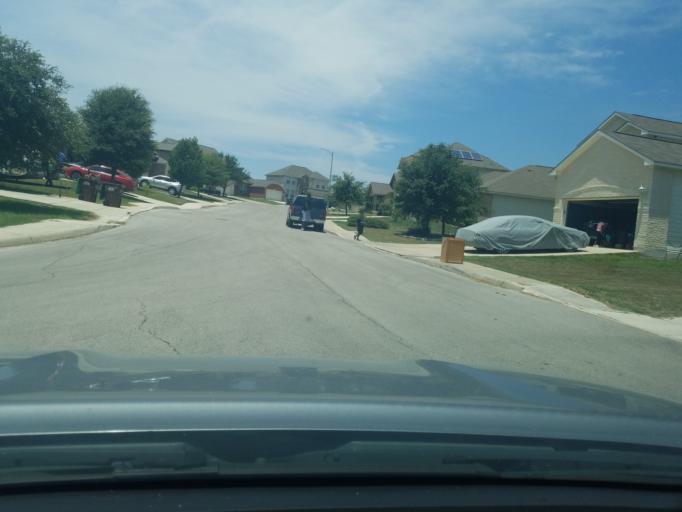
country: US
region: Texas
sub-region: Bexar County
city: Kirby
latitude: 29.4644
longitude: -98.3307
